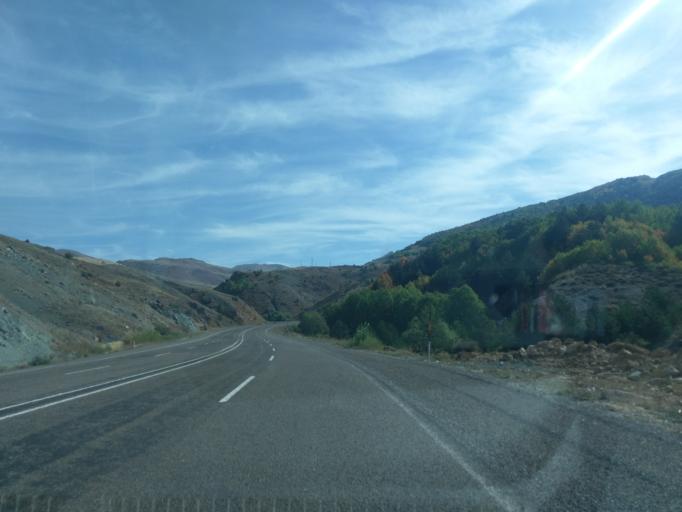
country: TR
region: Sivas
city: Imranli
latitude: 39.8567
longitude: 38.3107
